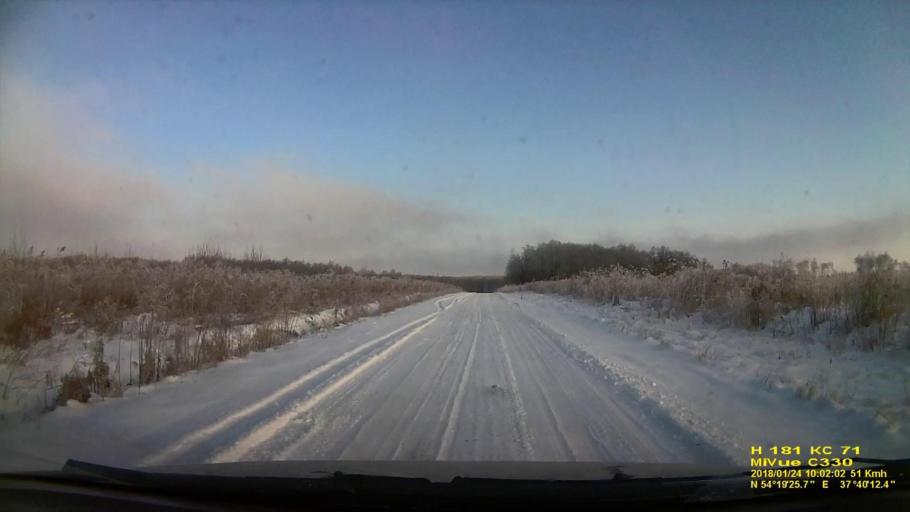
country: RU
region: Tula
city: Revyakino
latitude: 54.3239
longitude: 37.6702
